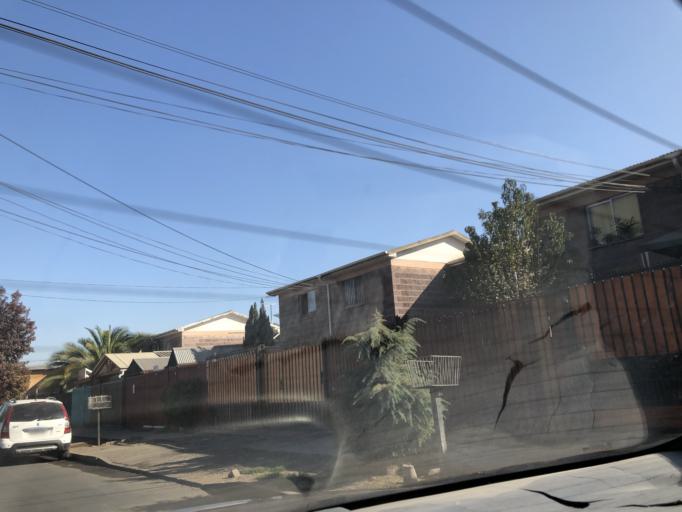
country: CL
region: Santiago Metropolitan
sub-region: Provincia de Santiago
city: La Pintana
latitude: -33.5760
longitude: -70.6011
